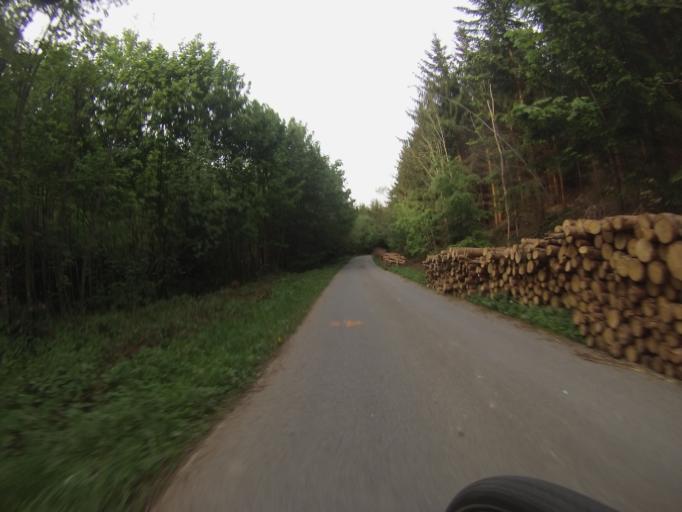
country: CZ
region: Olomoucky
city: Protivanov
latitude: 49.4705
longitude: 16.8823
